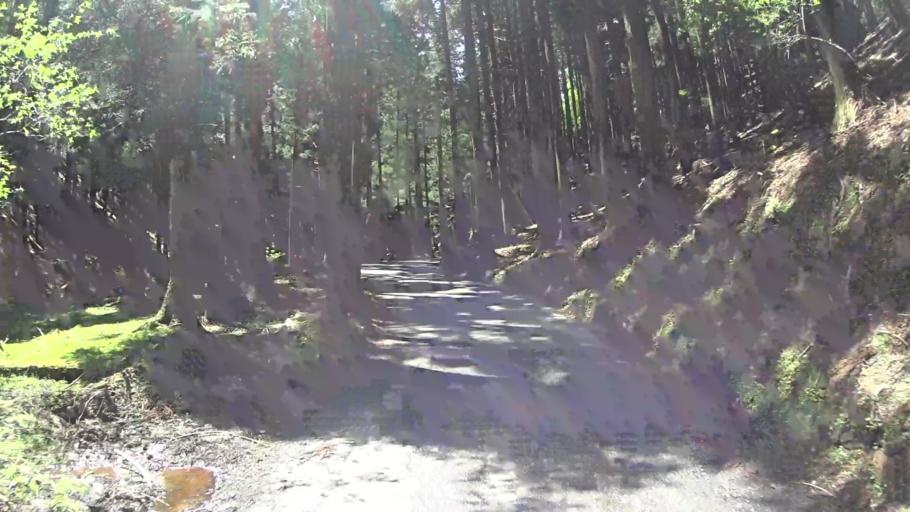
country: JP
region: Shiga Prefecture
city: Kitahama
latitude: 35.1598
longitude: 135.8010
